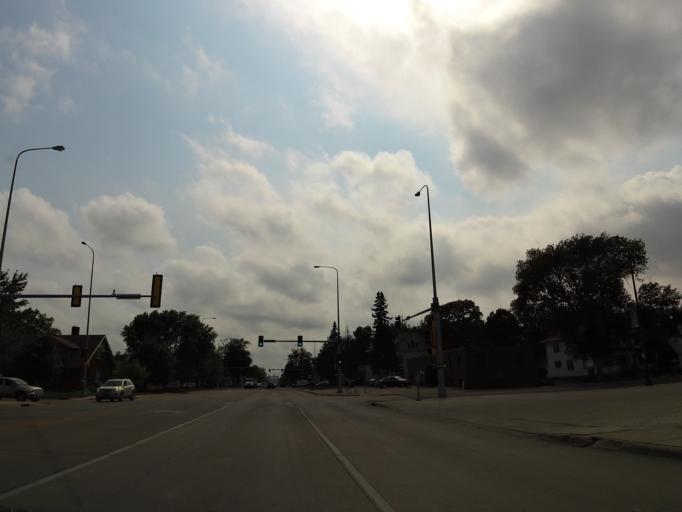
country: US
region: South Dakota
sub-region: Codington County
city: Watertown
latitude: 44.8993
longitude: -97.1064
